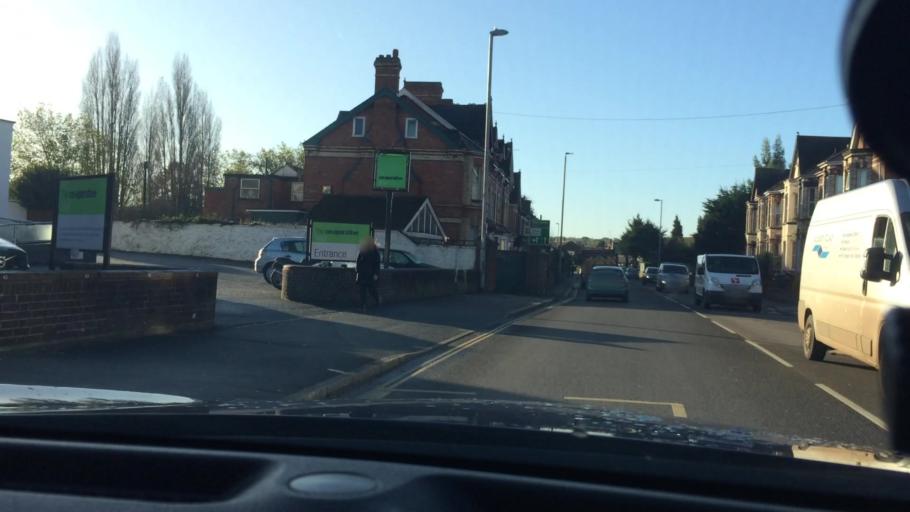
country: GB
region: England
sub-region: Devon
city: Exeter
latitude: 50.7107
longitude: -3.5379
